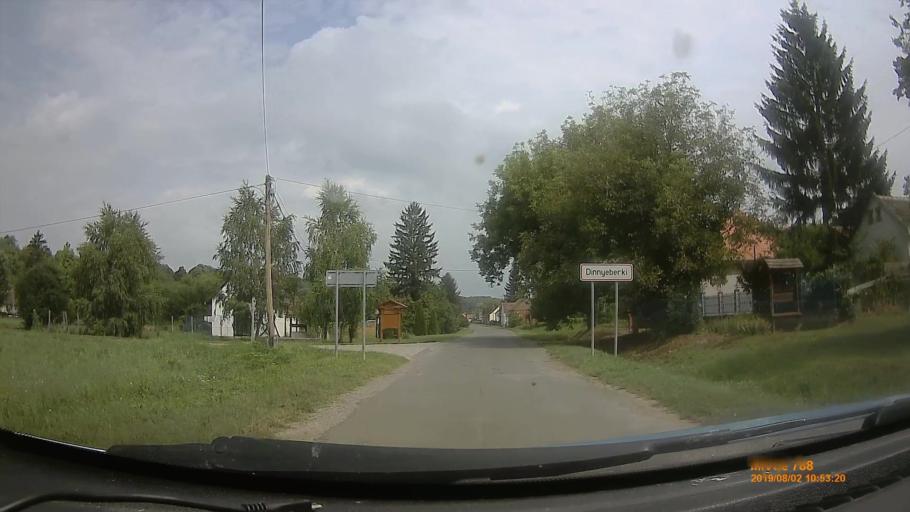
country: HU
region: Baranya
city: Buekkoesd
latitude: 46.0949
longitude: 17.9571
